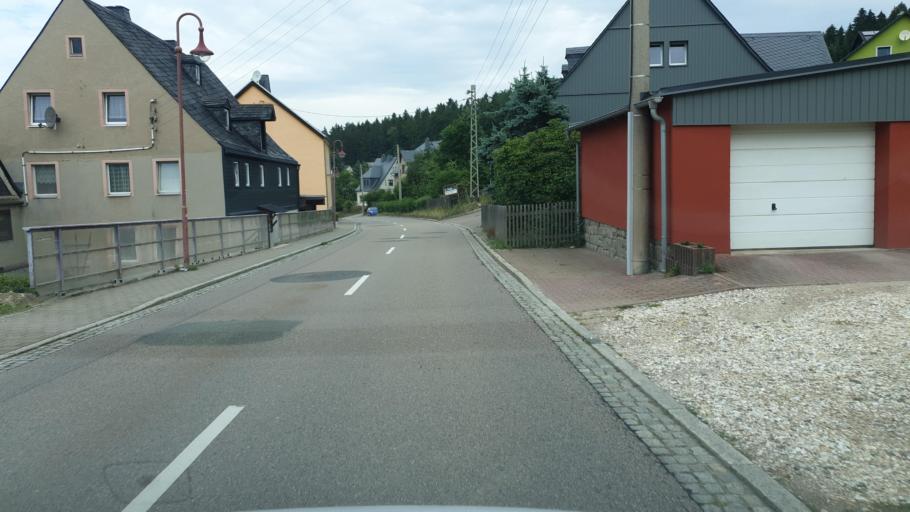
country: DE
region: Saxony
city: Bernsbach
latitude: 50.5851
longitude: 12.7589
